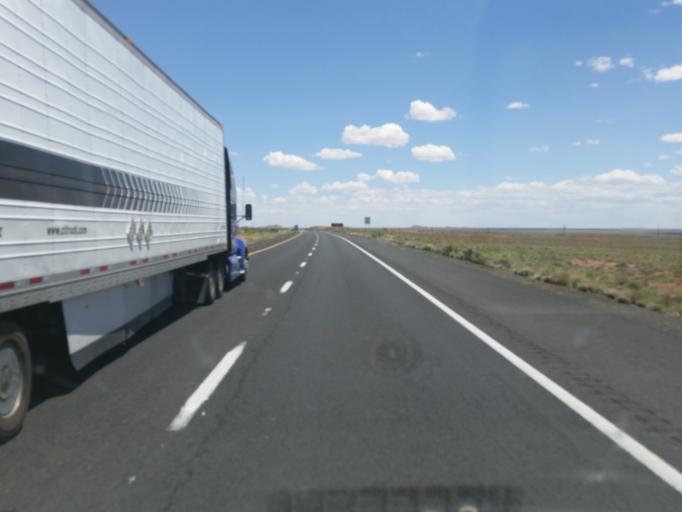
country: US
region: Arizona
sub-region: Navajo County
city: Joseph City
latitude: 34.9171
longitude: -110.2524
